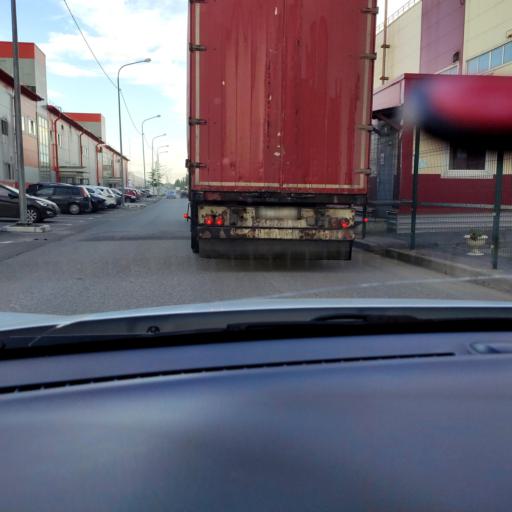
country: RU
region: Tatarstan
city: Staroye Arakchino
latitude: 55.8316
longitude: 49.0377
